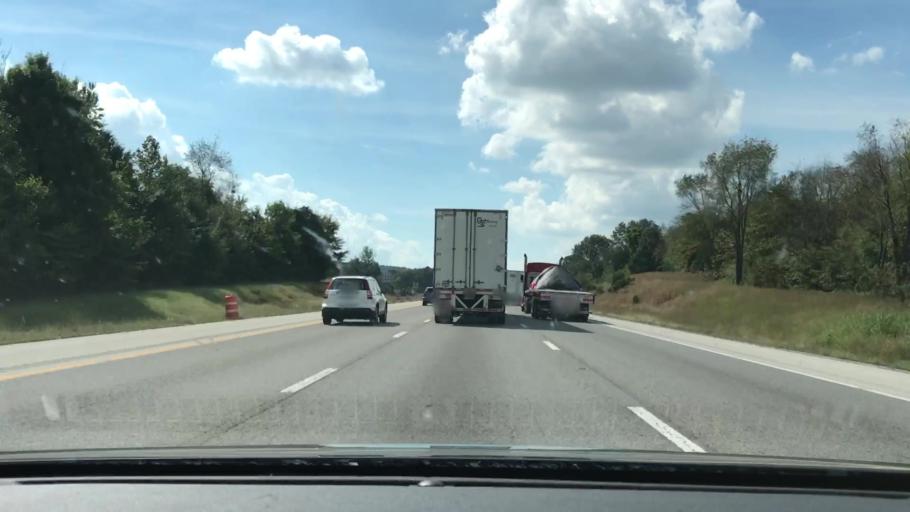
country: US
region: Kentucky
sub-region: Edmonson County
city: Brownsville
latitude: 37.0494
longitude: -86.1486
